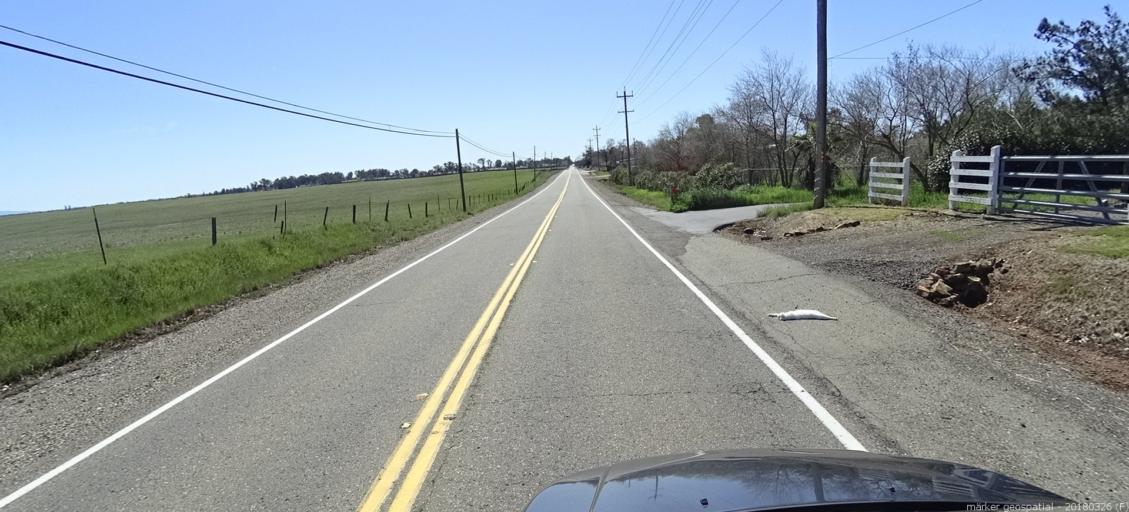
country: US
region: California
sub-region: Sacramento County
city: Vineyard
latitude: 38.4775
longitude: -121.2977
